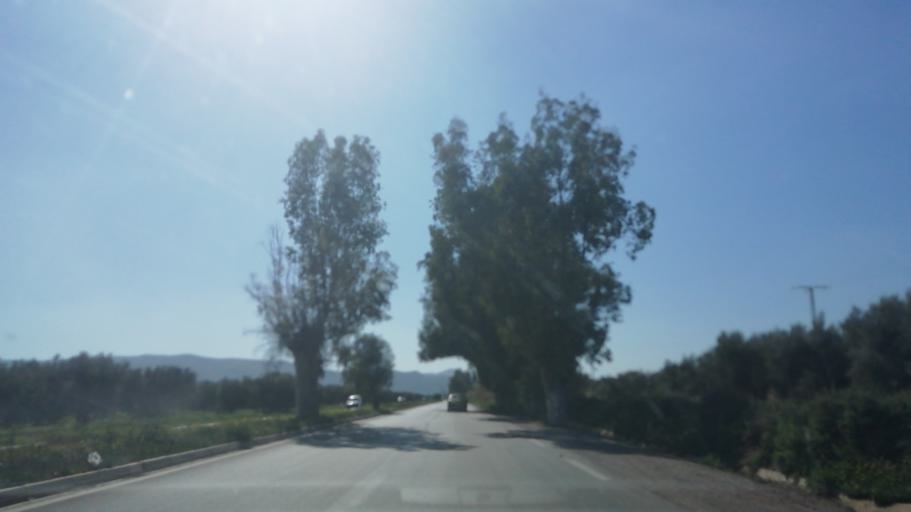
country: DZ
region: Mascara
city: Sig
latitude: 35.5514
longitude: -0.2063
